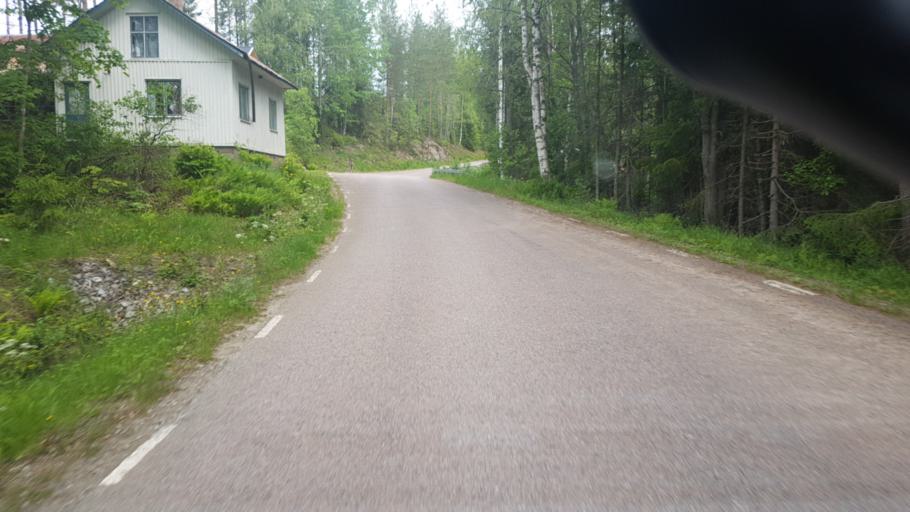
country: SE
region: Vaermland
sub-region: Arvika Kommun
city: Arvika
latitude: 59.7949
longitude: 12.8385
